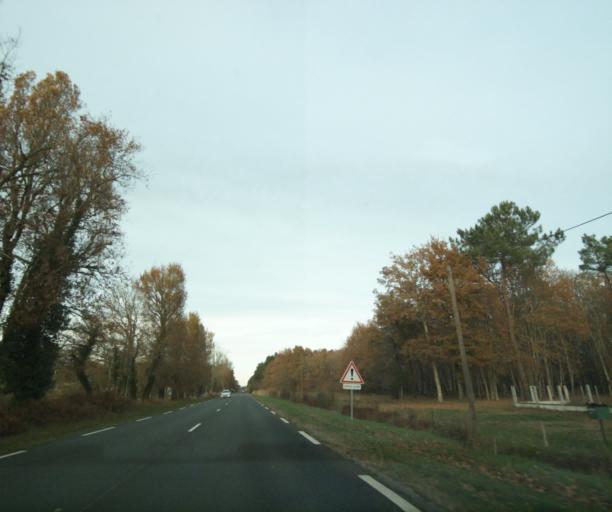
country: FR
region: Aquitaine
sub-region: Departement de la Gironde
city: Bazas
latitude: 44.3017
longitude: -0.2556
